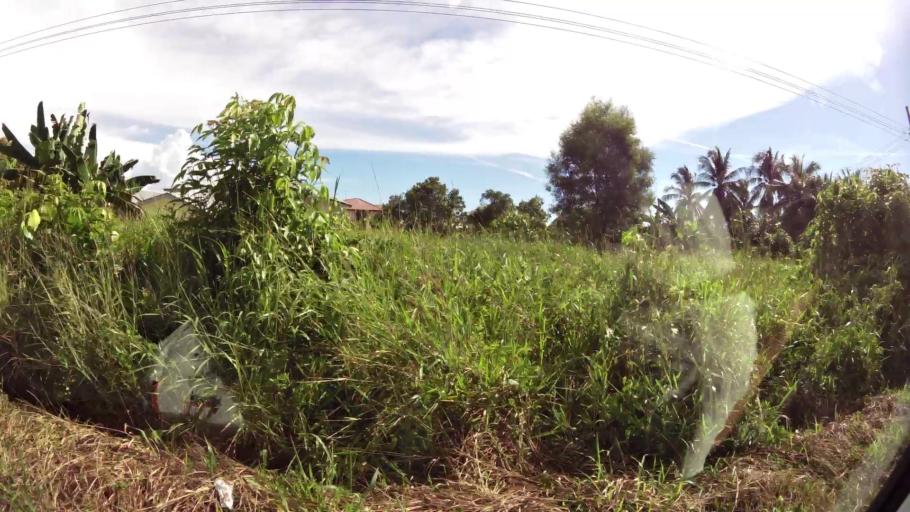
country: BN
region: Brunei and Muara
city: Bandar Seri Begawan
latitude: 5.0241
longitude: 115.0451
